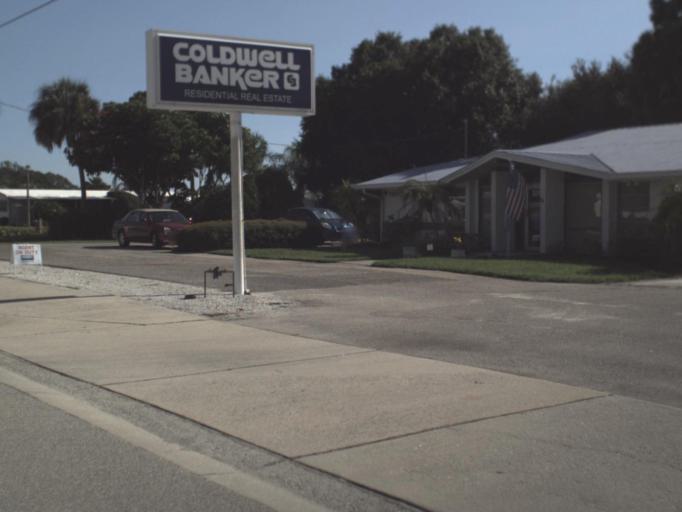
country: US
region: Florida
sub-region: Sarasota County
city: Englewood
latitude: 26.9954
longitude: -82.3724
